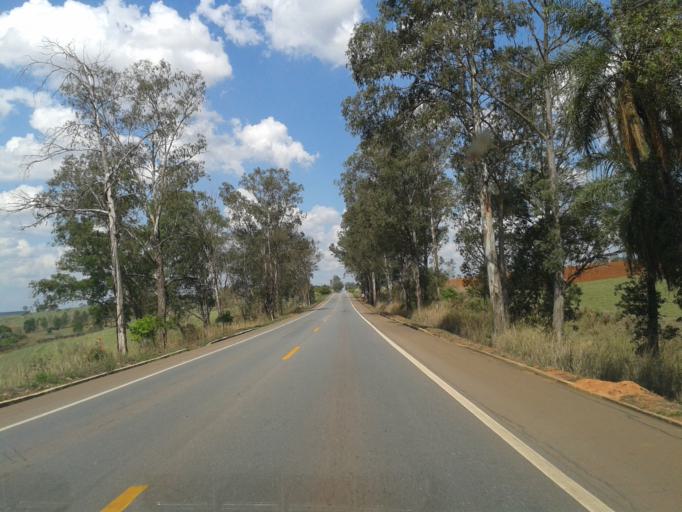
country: BR
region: Minas Gerais
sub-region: Luz
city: Luz
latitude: -19.7781
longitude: -45.7431
